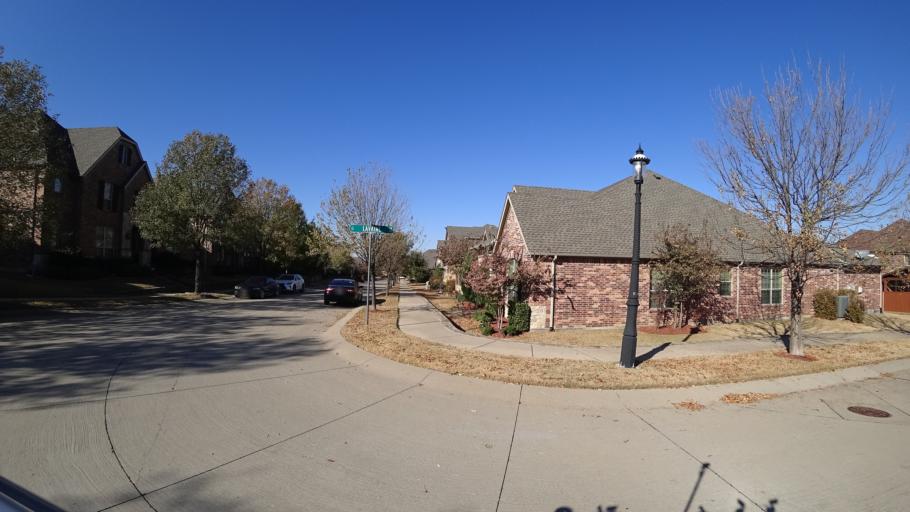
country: US
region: Texas
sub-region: Denton County
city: The Colony
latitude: 33.0405
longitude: -96.9192
